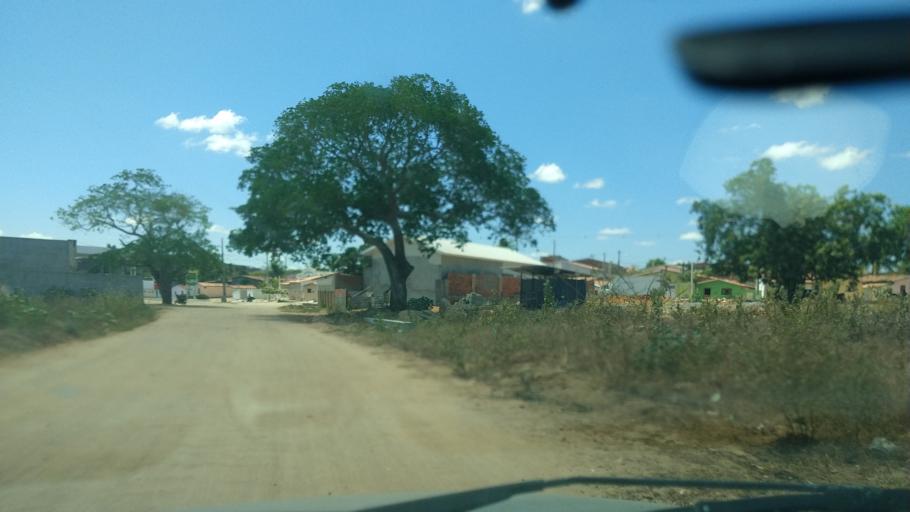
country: BR
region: Rio Grande do Norte
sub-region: Cerro Cora
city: Cerro Cora
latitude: -6.0347
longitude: -36.3457
